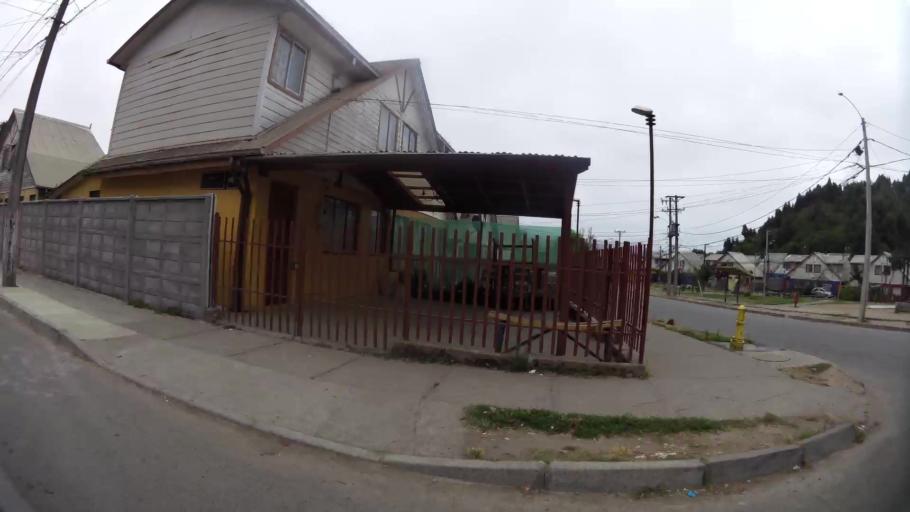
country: CL
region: Biobio
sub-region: Provincia de Concepcion
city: Concepcion
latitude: -36.8200
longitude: -72.9860
